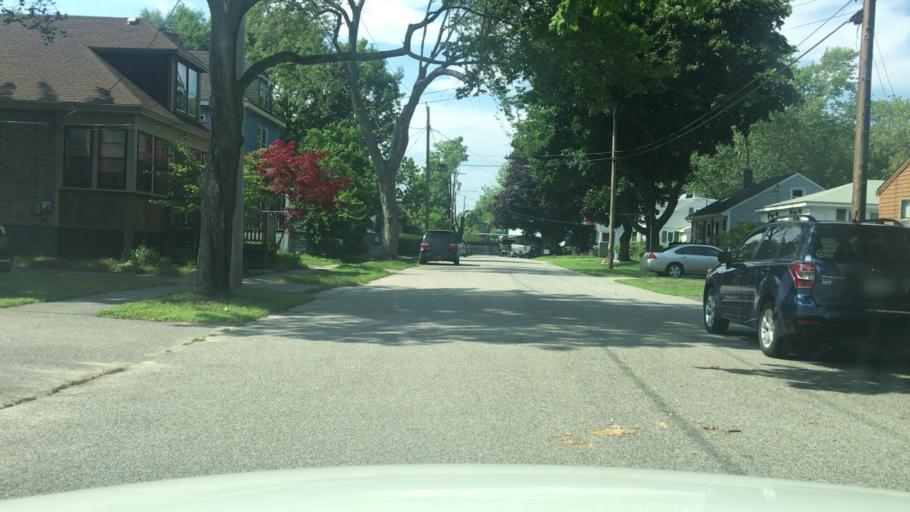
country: US
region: Maine
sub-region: Cumberland County
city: South Portland
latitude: 43.6316
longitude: -70.2716
